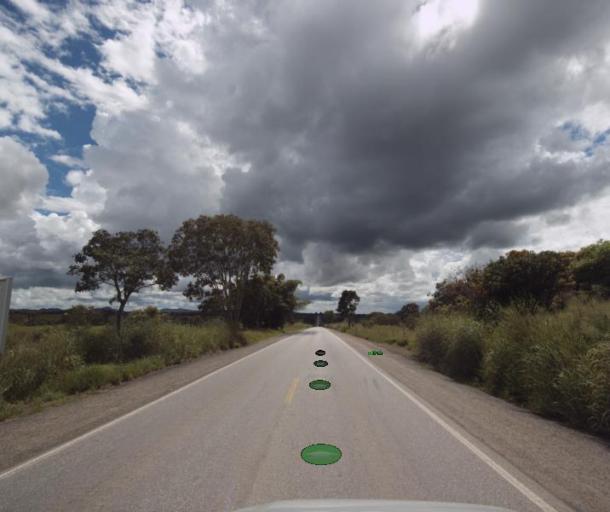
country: BR
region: Goias
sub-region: Uruacu
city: Uruacu
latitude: -14.2725
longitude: -49.1458
